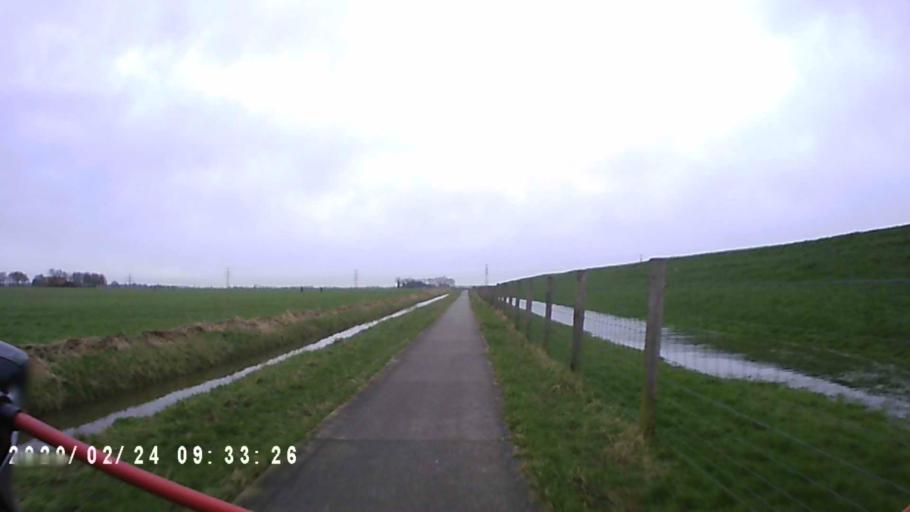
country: NL
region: Groningen
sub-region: Gemeente Winsum
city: Winsum
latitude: 53.3016
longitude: 6.4996
